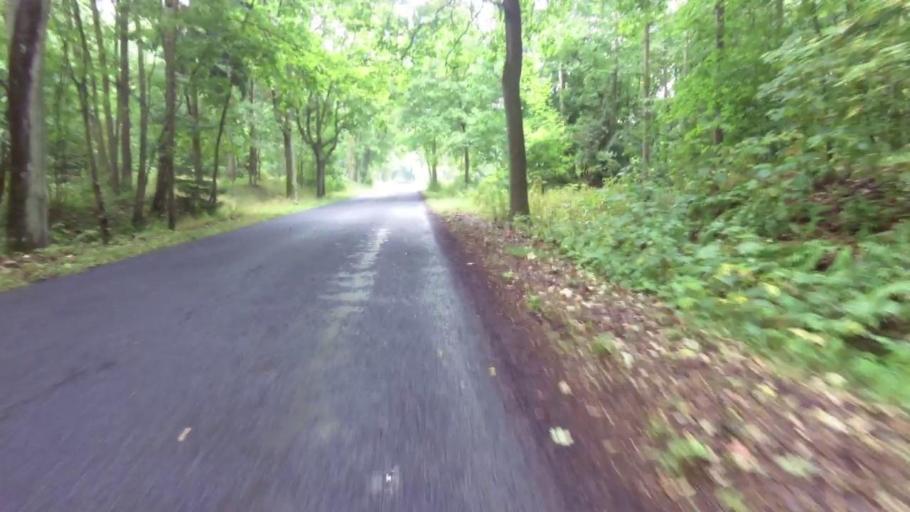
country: PL
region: West Pomeranian Voivodeship
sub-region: Powiat choszczenski
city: Choszczno
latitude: 53.2216
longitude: 15.3825
